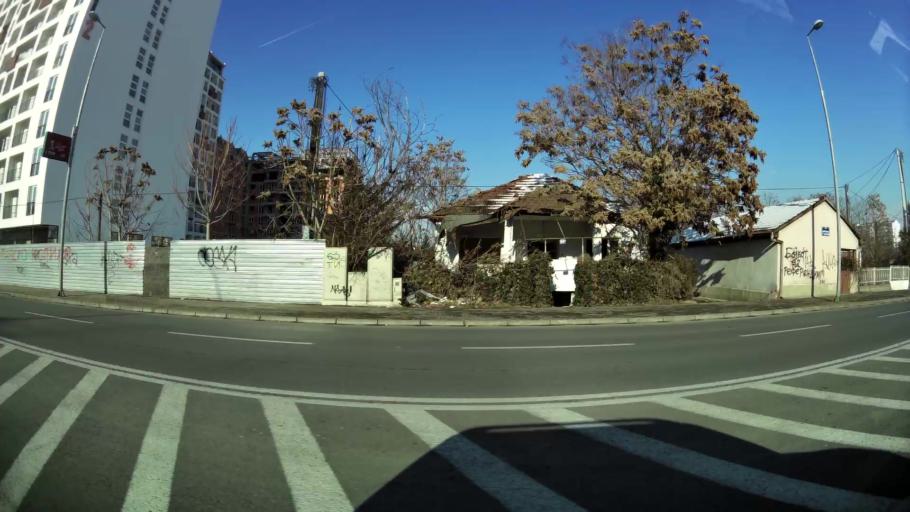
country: MK
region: Karpos
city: Skopje
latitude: 41.9971
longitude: 21.3988
